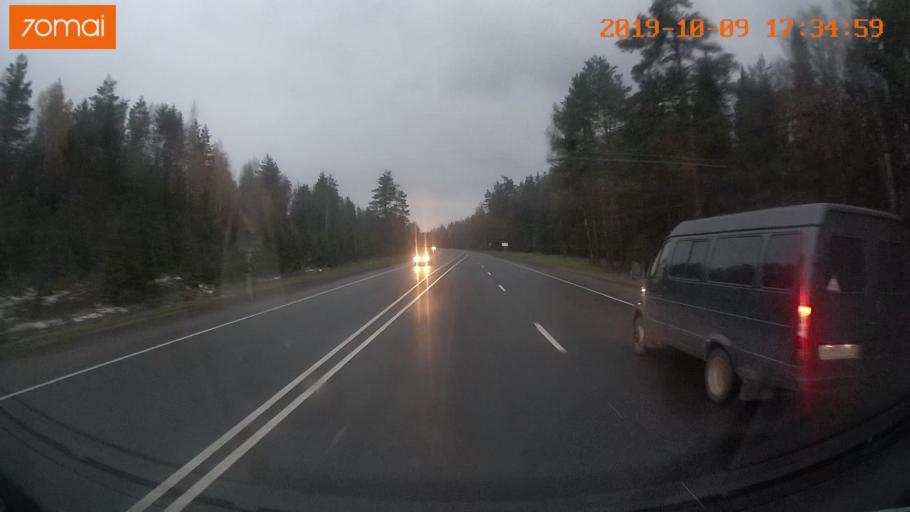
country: RU
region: Ivanovo
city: Bogorodskoye
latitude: 57.1004
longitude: 41.0063
